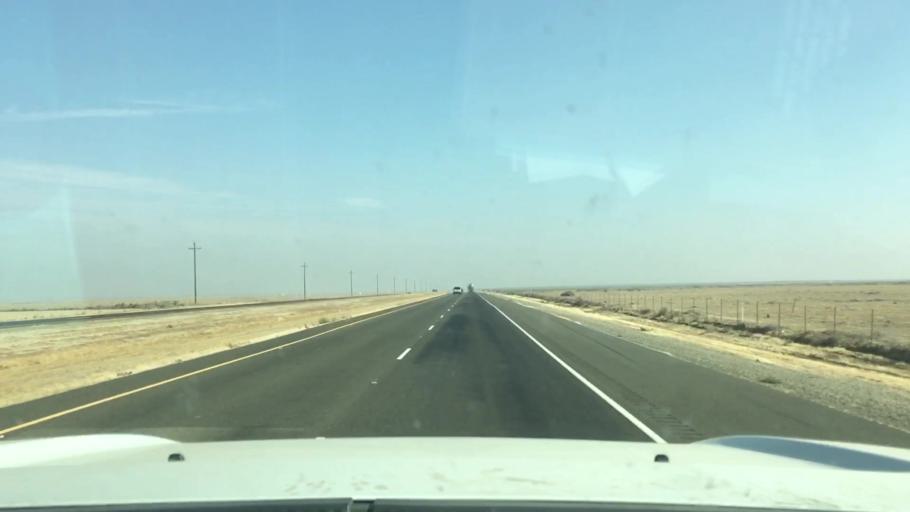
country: US
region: California
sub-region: Kern County
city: Lost Hills
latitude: 35.6156
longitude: -119.7914
